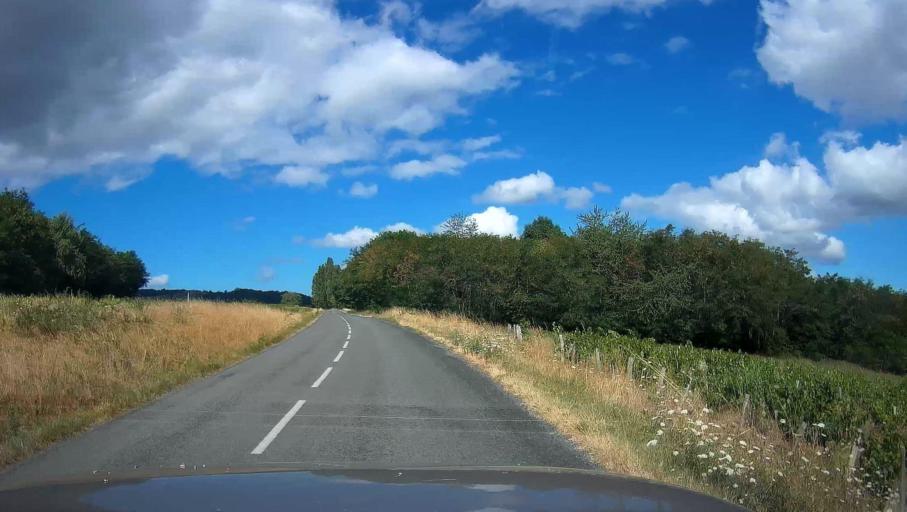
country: FR
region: Rhone-Alpes
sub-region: Departement du Rhone
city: Cogny
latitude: 45.9742
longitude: 4.6239
